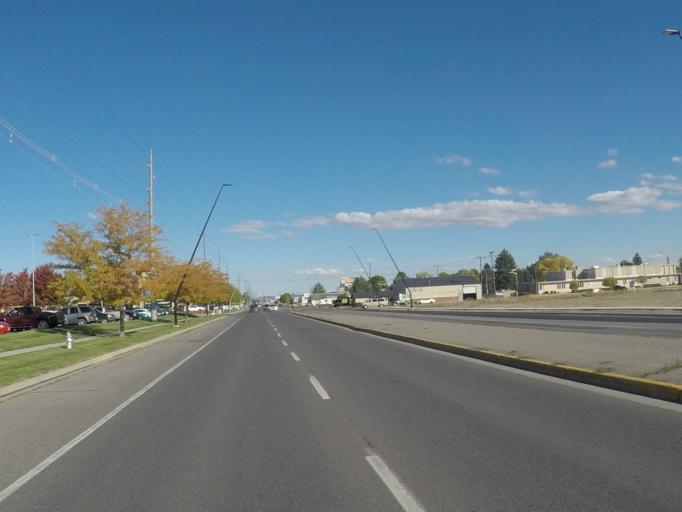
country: US
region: Montana
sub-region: Yellowstone County
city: Billings
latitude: 45.7842
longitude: -108.5935
